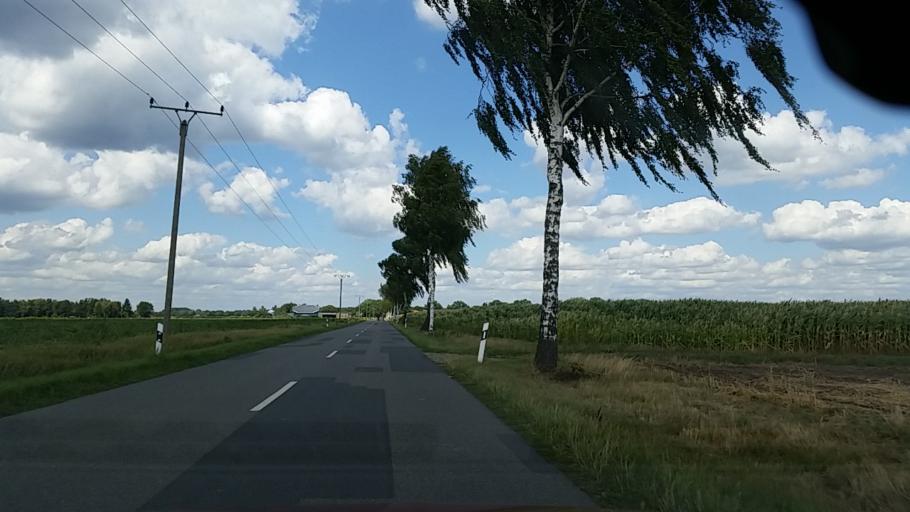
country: DE
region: Lower Saxony
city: Sprakensehl
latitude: 52.7434
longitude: 10.5146
